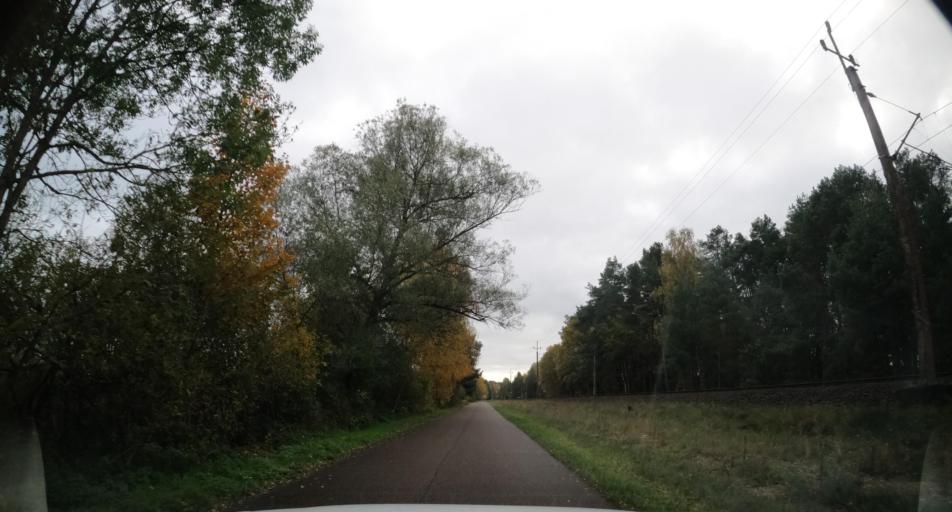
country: PL
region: West Pomeranian Voivodeship
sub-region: Powiat kamienski
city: Wolin
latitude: 53.9220
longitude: 14.5544
